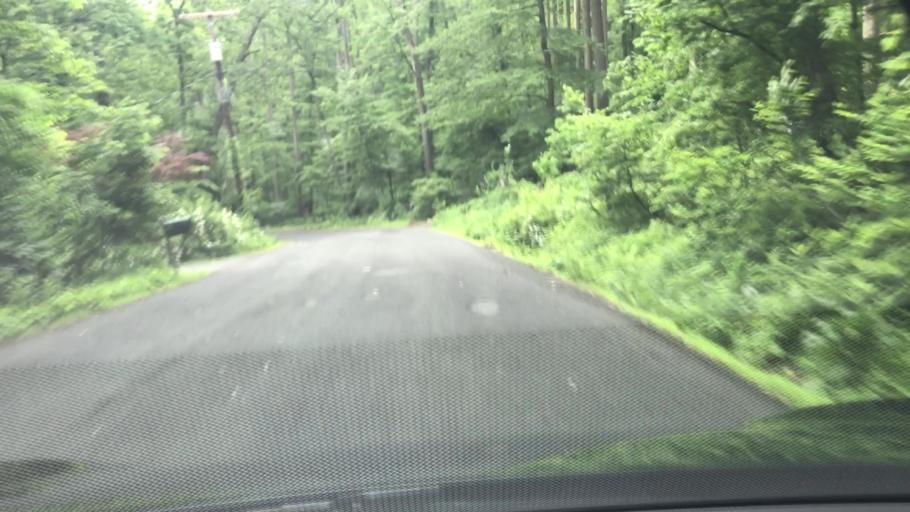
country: US
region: New Jersey
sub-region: Hunterdon County
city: Lebanon
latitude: 40.6297
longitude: -74.8078
